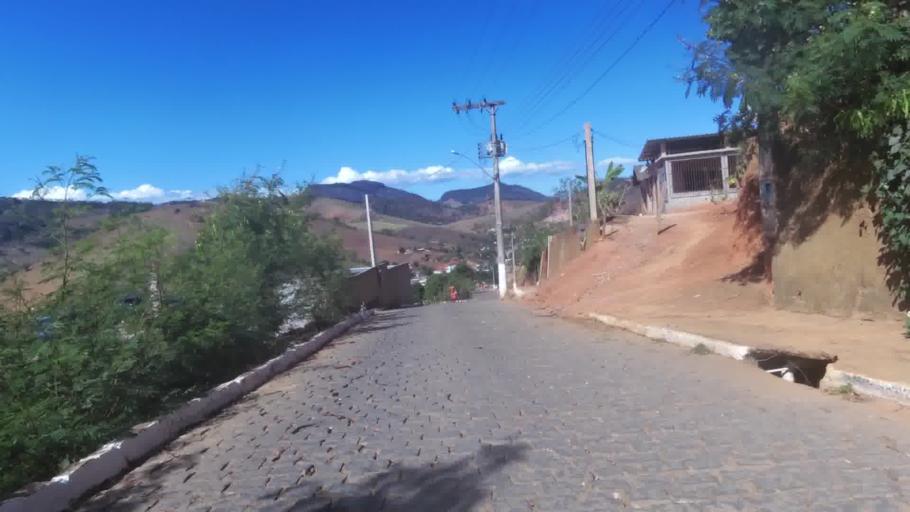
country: BR
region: Espirito Santo
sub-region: Cachoeiro De Itapemirim
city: Cachoeiro de Itapemirim
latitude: -20.9180
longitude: -41.1948
